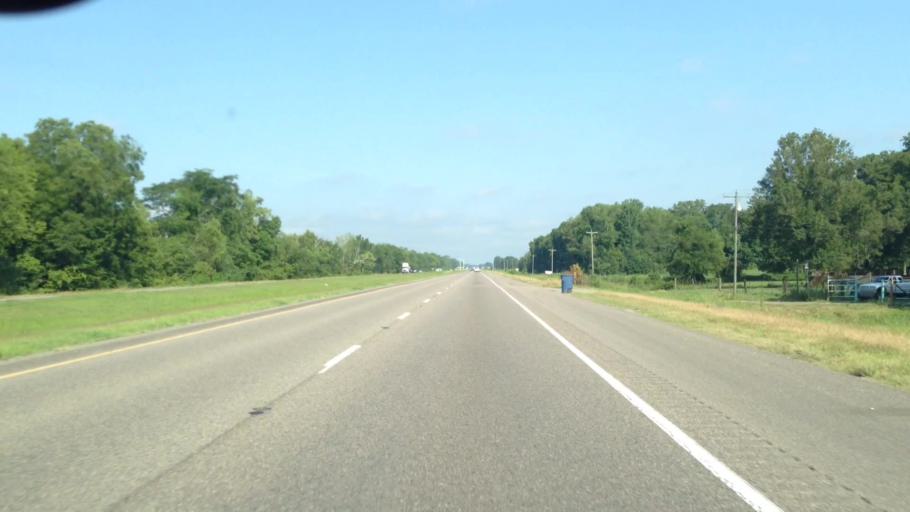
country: US
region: Louisiana
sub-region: West Baton Rouge Parish
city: Erwinville
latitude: 30.5160
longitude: -91.3562
